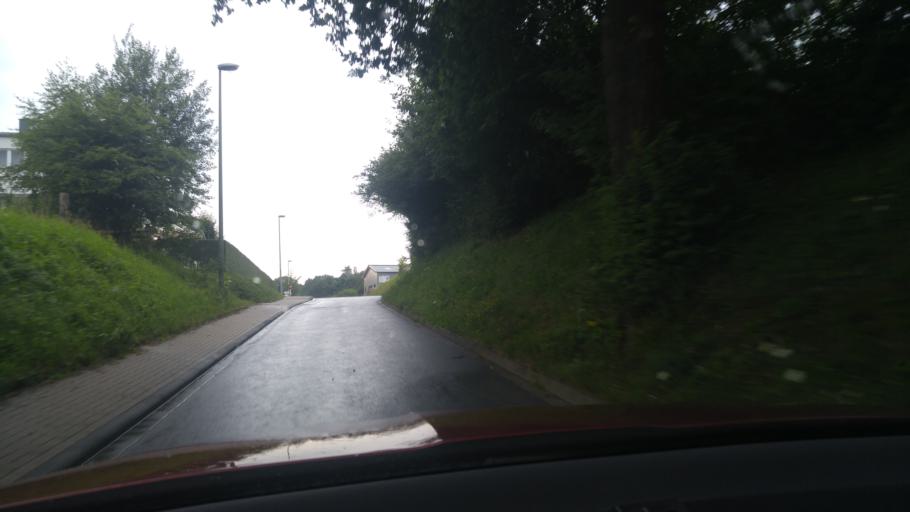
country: DE
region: North Rhine-Westphalia
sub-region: Regierungsbezirk Koln
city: Ruppichteroth
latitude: 50.8494
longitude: 7.4790
